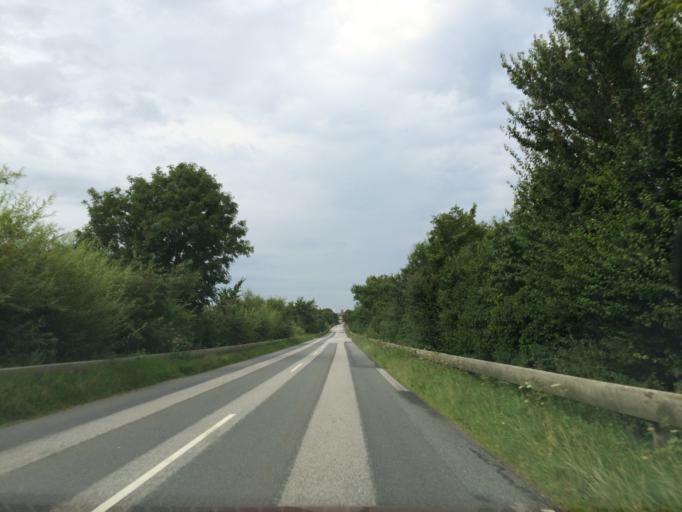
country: DK
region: South Denmark
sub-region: Sonderborg Kommune
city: Broager
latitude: 54.9022
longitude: 9.6749
